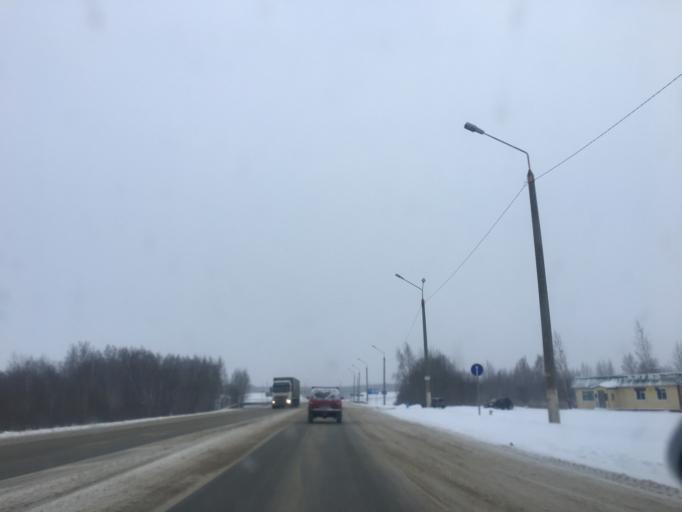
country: RU
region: Tula
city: Kosaya Gora
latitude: 54.1618
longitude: 37.4960
